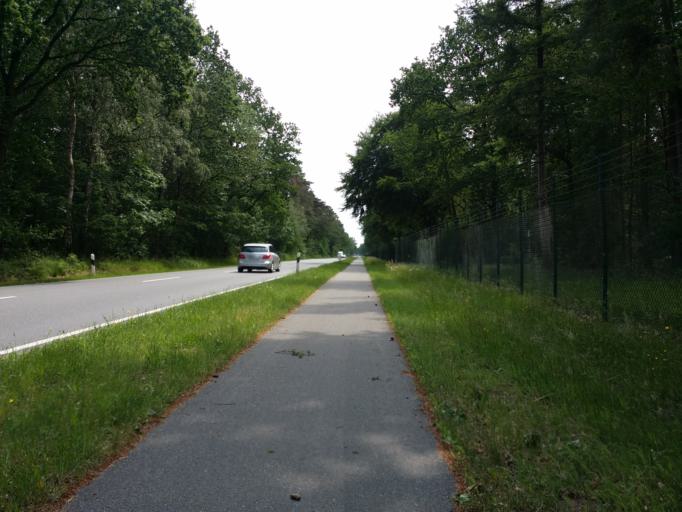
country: DE
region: Lower Saxony
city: Zetel
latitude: 53.4050
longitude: 7.9076
